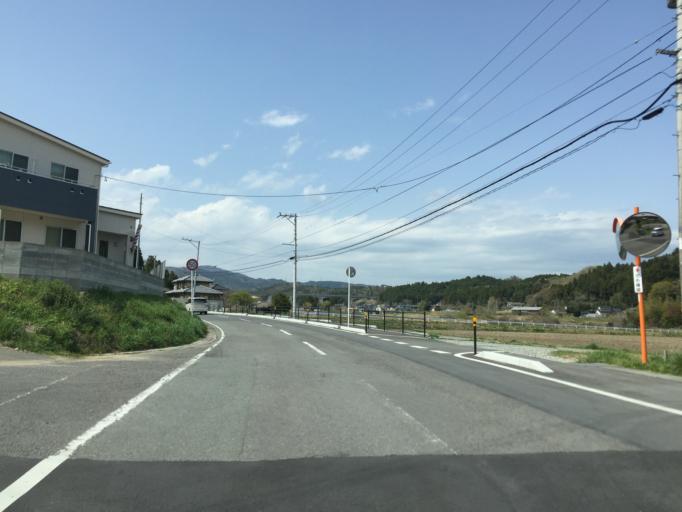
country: JP
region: Fukushima
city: Iwaki
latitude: 37.1611
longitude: 140.9745
